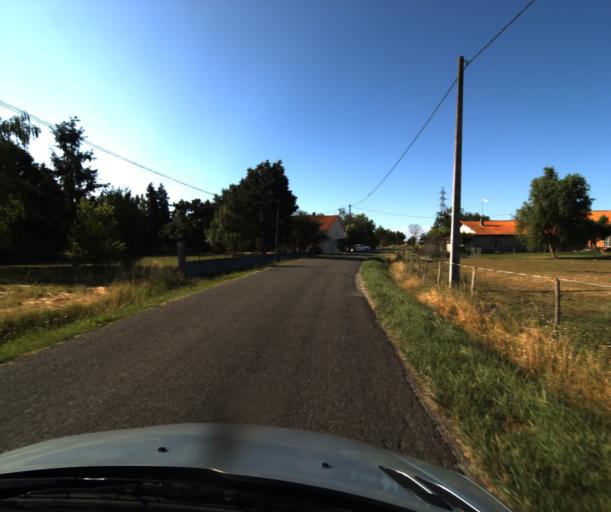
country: FR
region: Midi-Pyrenees
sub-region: Departement du Tarn-et-Garonne
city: Saint-Porquier
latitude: 44.0512
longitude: 1.2125
